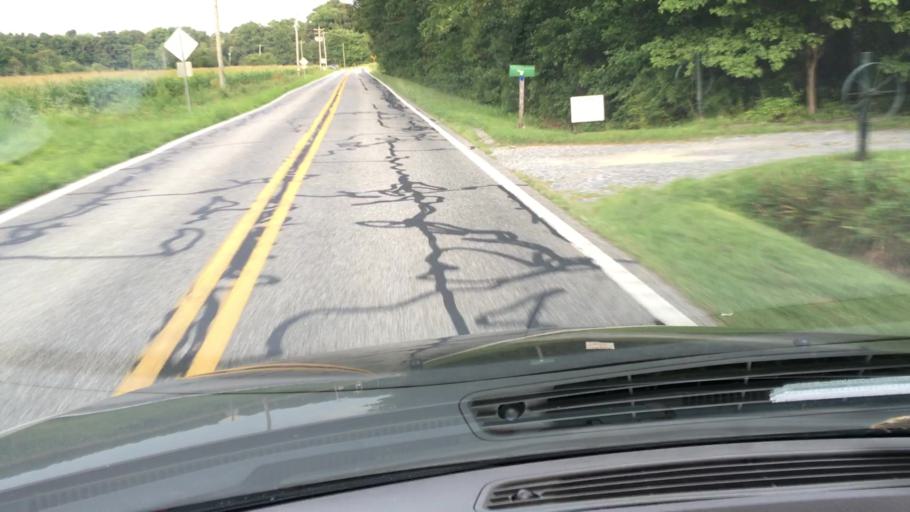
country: US
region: Delaware
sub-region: Sussex County
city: Ocean View
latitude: 38.5137
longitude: -75.0964
